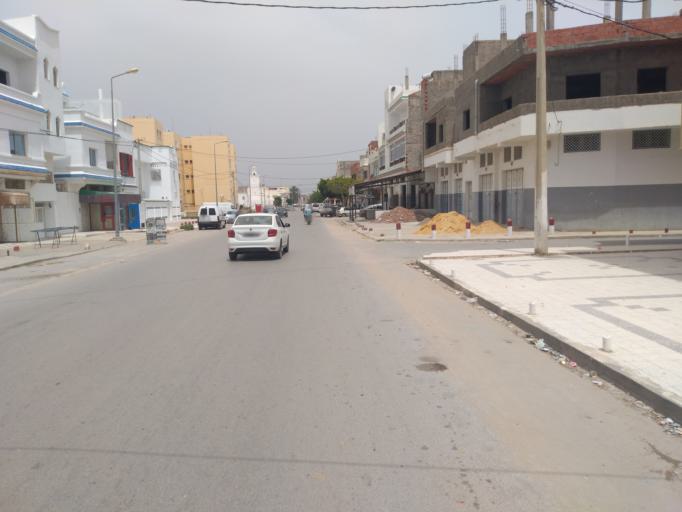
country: TN
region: Al Qayrawan
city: Kairouan
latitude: 35.6698
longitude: 10.0887
